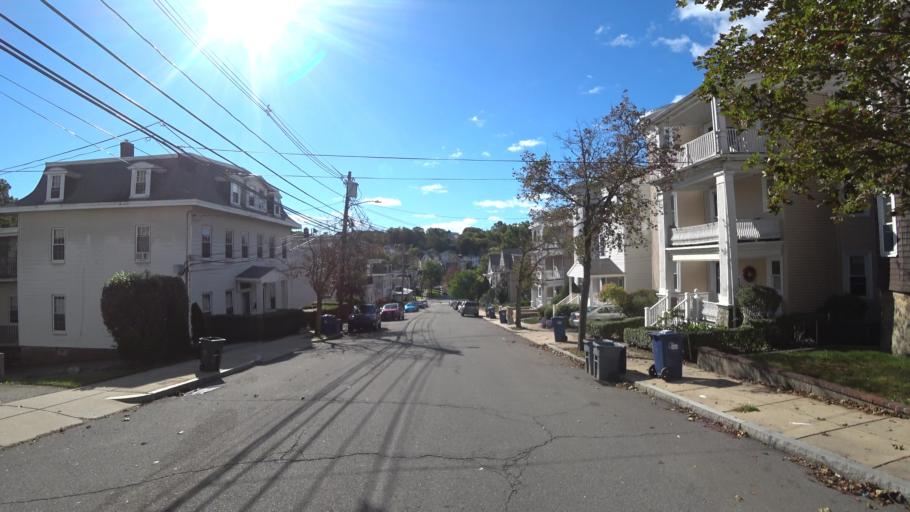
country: US
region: Massachusetts
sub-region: Middlesex County
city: Watertown
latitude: 42.3523
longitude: -71.1678
